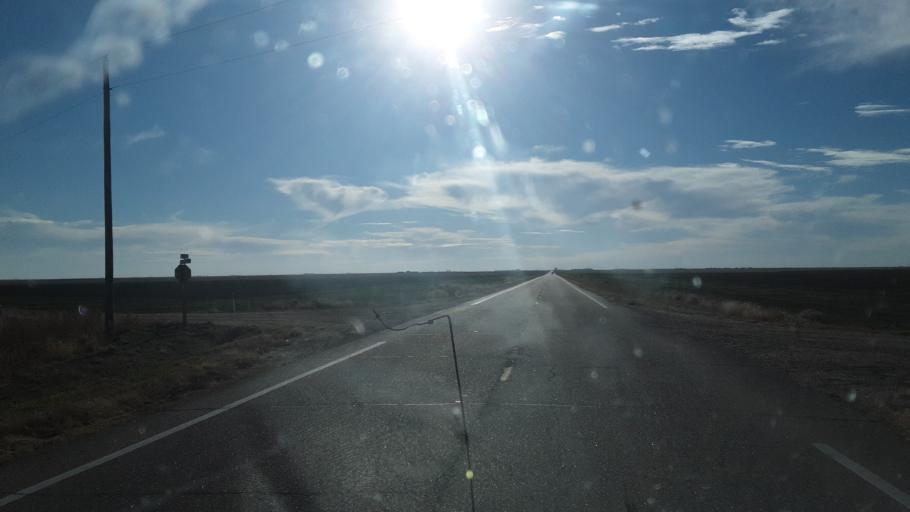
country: US
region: Kansas
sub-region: Finney County
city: Garden City
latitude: 38.0582
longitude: -100.7003
